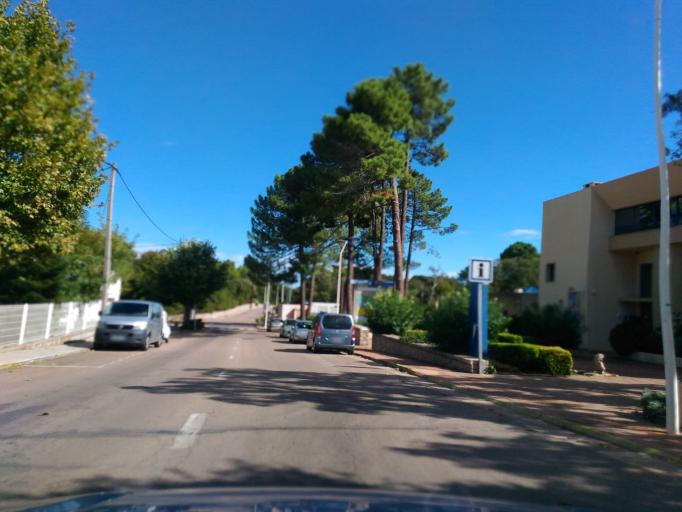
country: FR
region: Corsica
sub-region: Departement de la Corse-du-Sud
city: Porto-Vecchio
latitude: 41.6993
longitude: 9.3492
